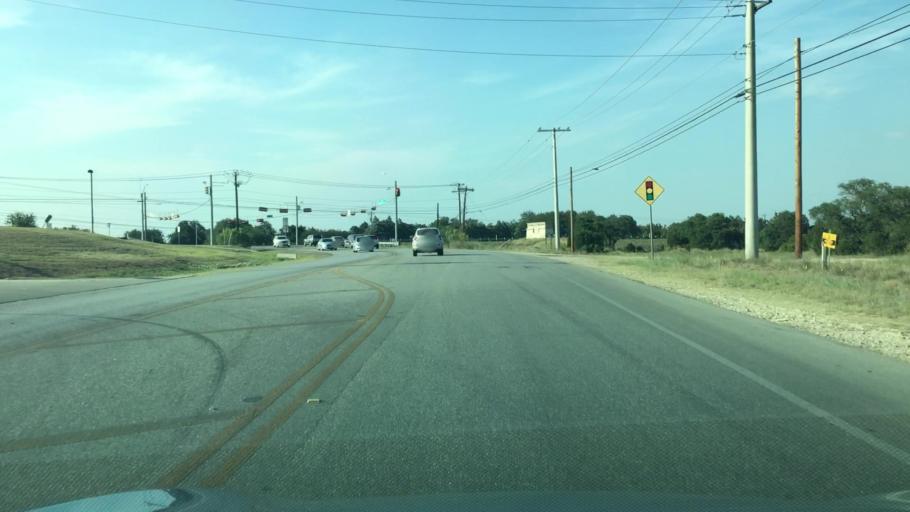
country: US
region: Texas
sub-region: Hays County
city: Dripping Springs
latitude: 30.1954
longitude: -97.9976
